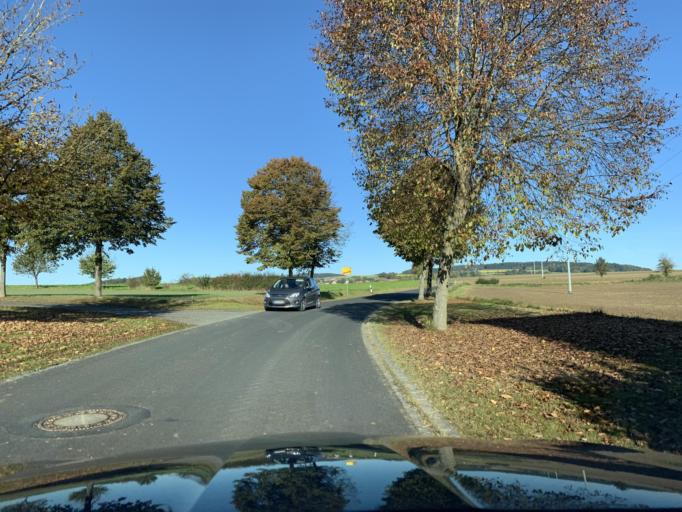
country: DE
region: Bavaria
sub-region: Upper Palatinate
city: Thanstein
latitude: 49.3949
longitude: 12.4725
